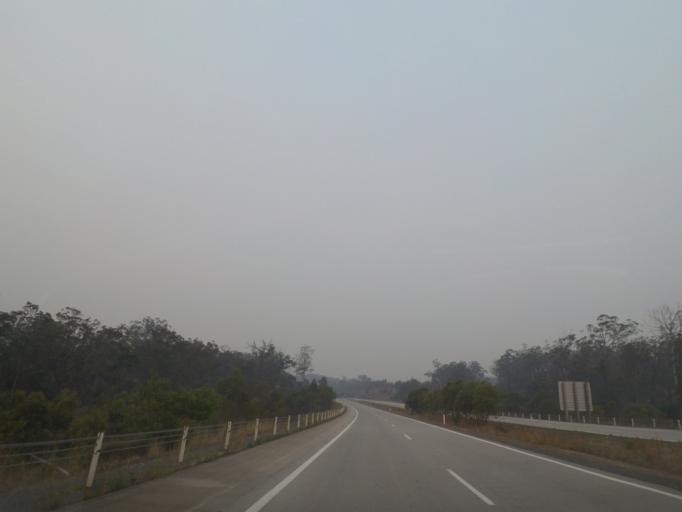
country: AU
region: New South Wales
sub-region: Kempsey
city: Kempsey
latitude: -31.1085
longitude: 152.8413
